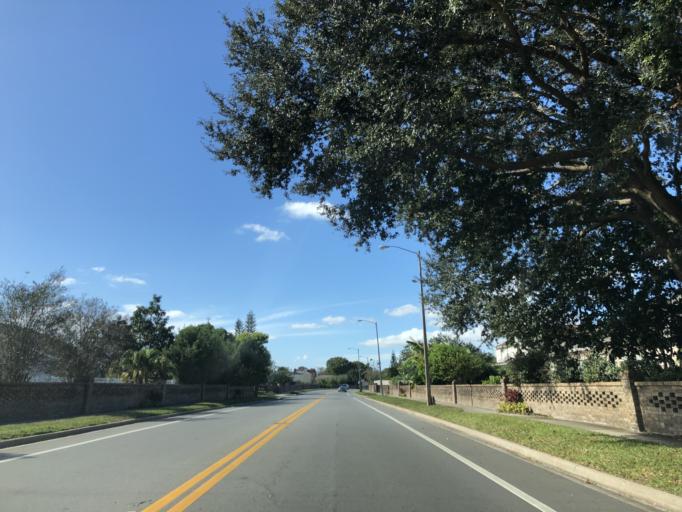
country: US
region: Florida
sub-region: Orange County
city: Hunters Creek
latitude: 28.3787
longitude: -81.4067
